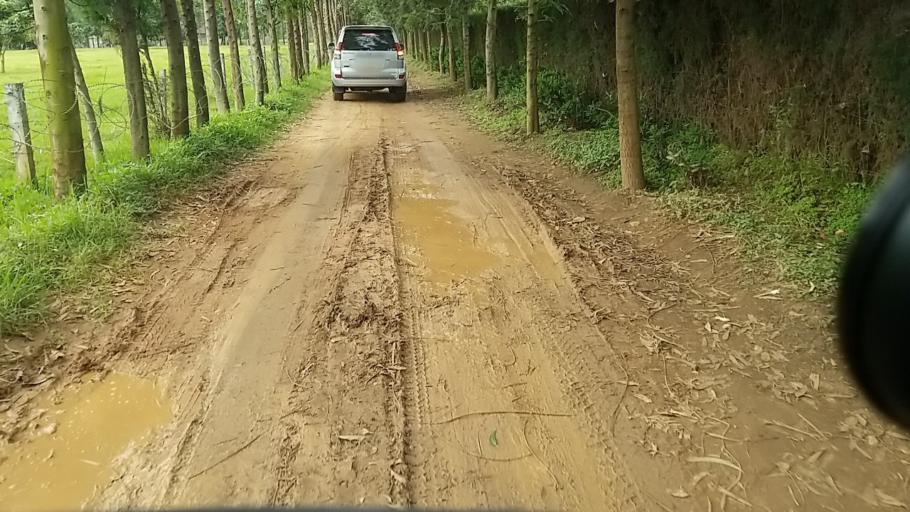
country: CD
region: Nord Kivu
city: Sake
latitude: -1.5657
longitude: 29.0433
